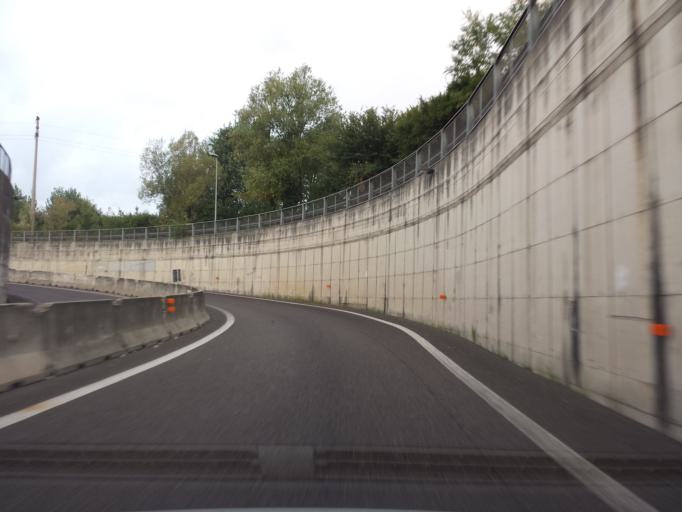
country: IT
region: Veneto
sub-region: Provincia di Padova
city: Saletto
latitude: 45.4481
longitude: 11.8609
